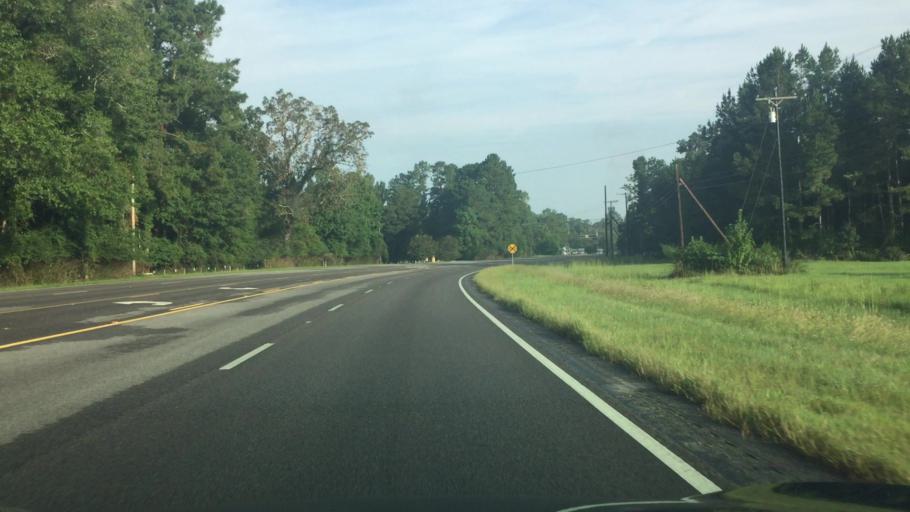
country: US
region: Alabama
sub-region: Covington County
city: Andalusia
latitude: 31.3341
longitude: -86.5183
